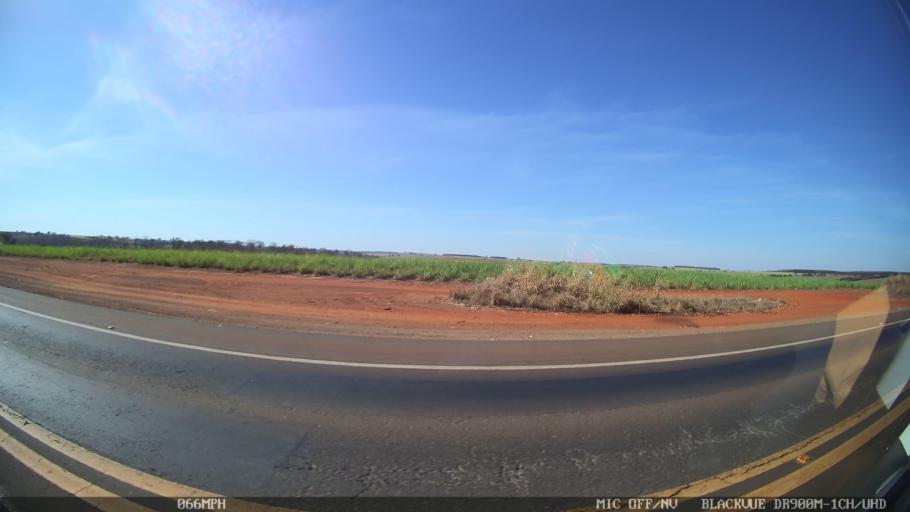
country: BR
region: Sao Paulo
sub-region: Olimpia
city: Olimpia
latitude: -20.7113
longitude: -48.8791
